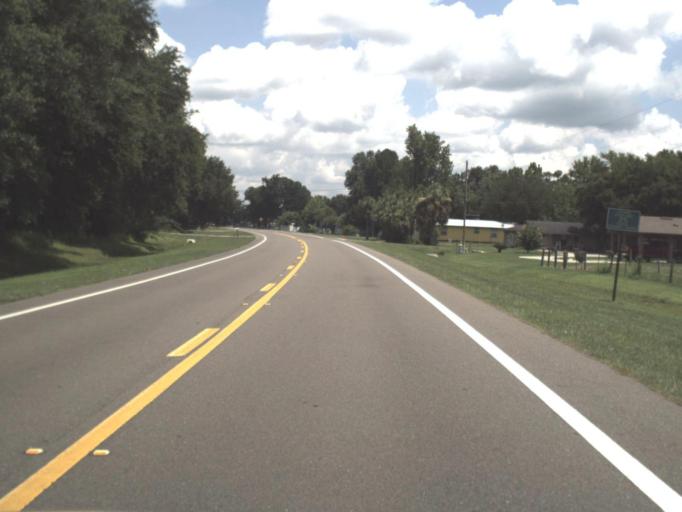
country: US
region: Florida
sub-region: Union County
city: Lake Butler
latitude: 30.0095
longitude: -82.3445
